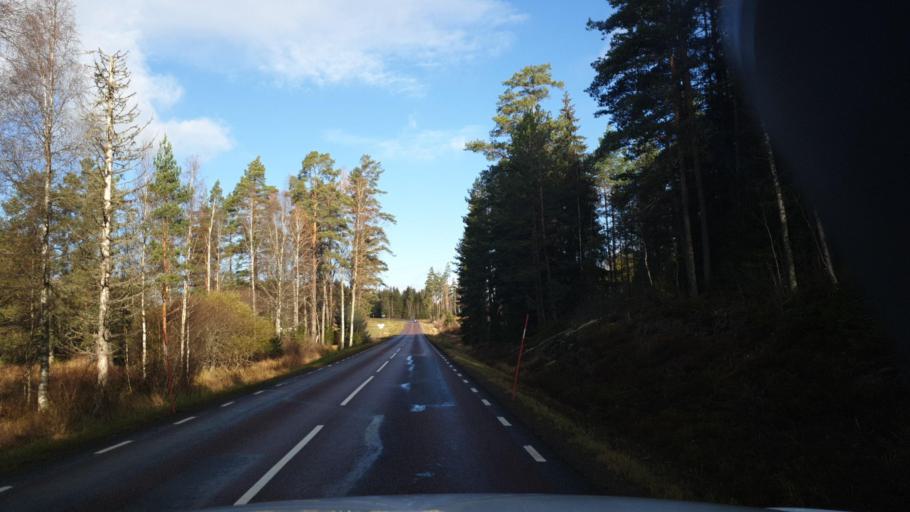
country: SE
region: Vaermland
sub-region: Grums Kommun
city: Grums
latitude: 59.4414
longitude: 12.9770
